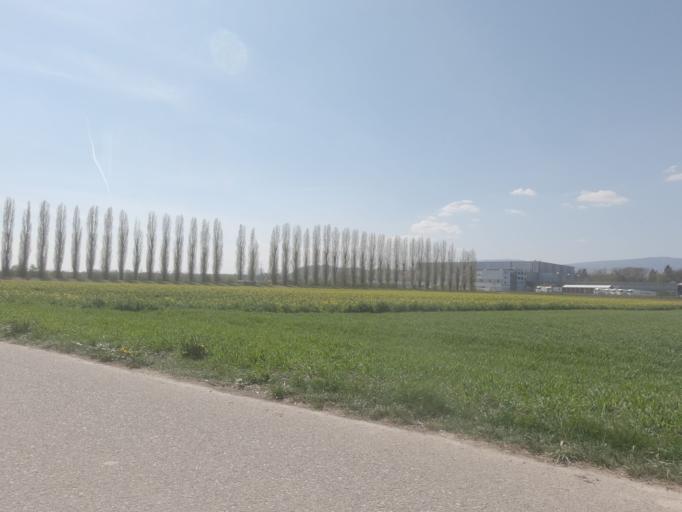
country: CH
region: Bern
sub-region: Biel/Bienne District
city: Orpund
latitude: 47.1155
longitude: 7.3386
